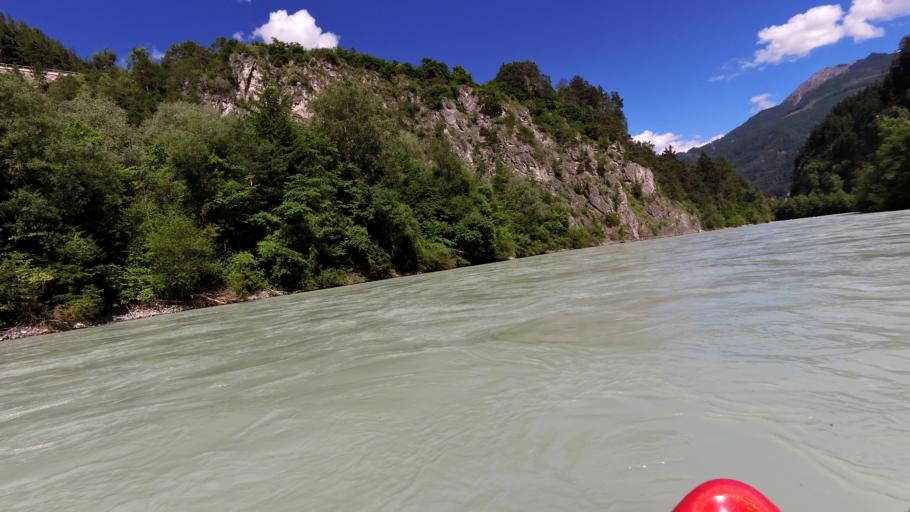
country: AT
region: Tyrol
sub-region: Politischer Bezirk Imst
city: Karrosten
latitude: 47.2184
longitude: 10.7671
